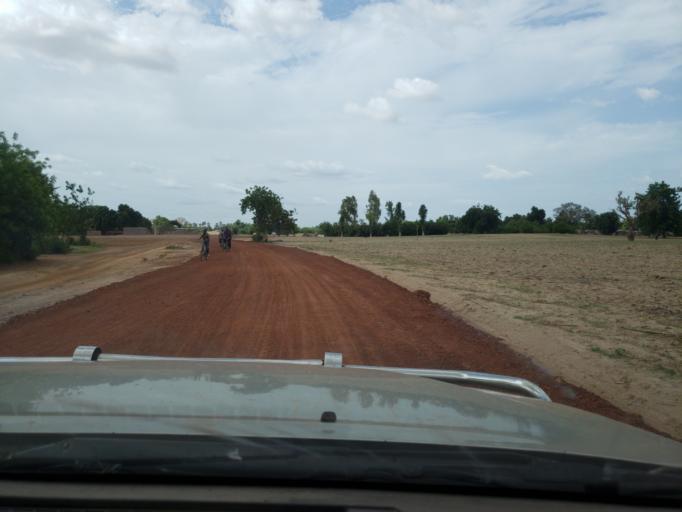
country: ML
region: Segou
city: Bla
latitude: 12.7287
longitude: -5.6722
